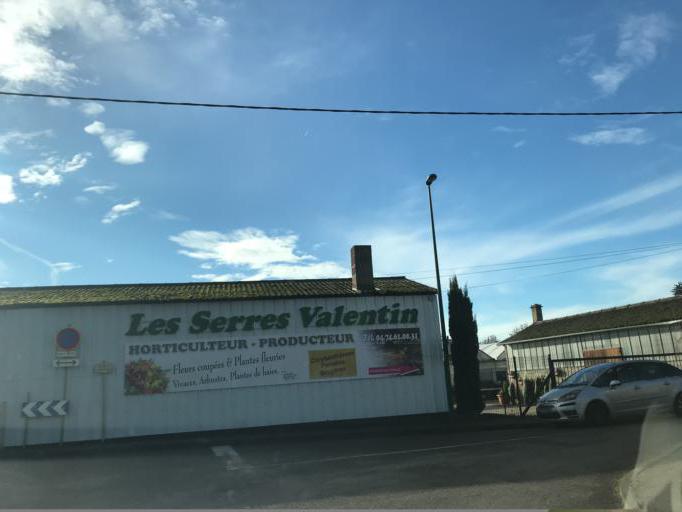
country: FR
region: Rhone-Alpes
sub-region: Departement de l'Ain
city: Meximieux
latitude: 45.9011
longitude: 5.1947
